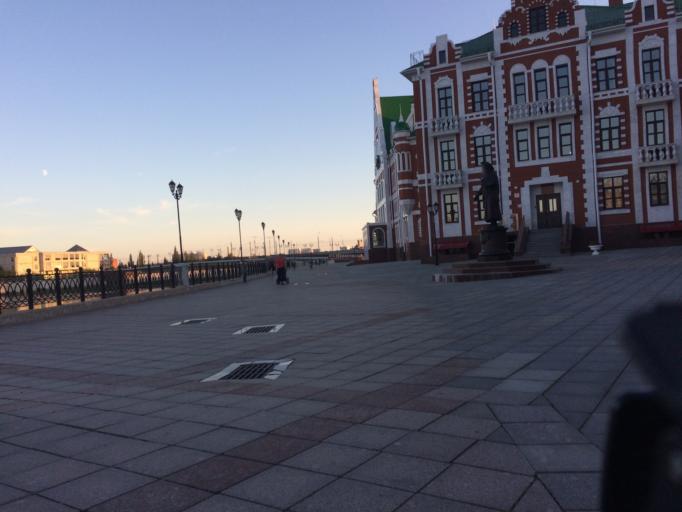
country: RU
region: Mariy-El
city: Yoshkar-Ola
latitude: 56.6314
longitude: 47.8992
